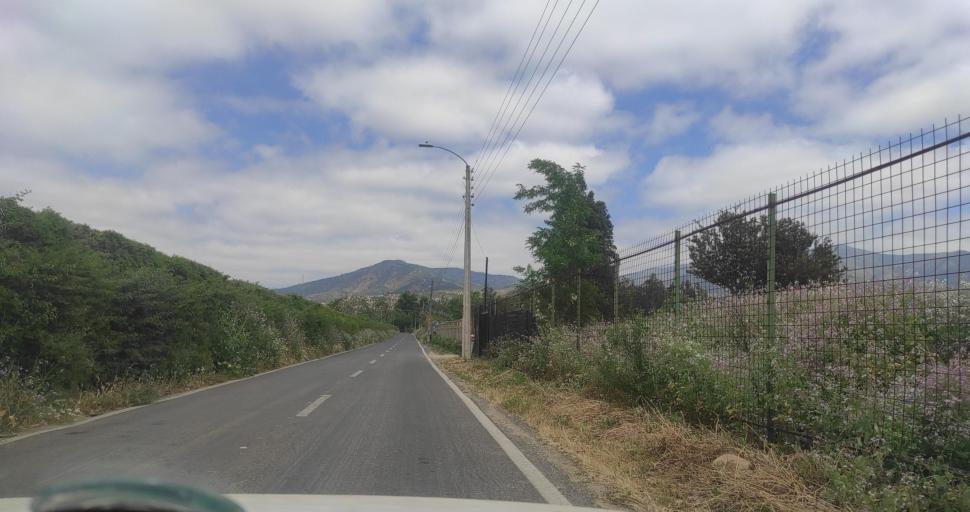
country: CL
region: Valparaiso
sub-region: Provincia de Marga Marga
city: Limache
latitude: -33.0352
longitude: -71.2315
